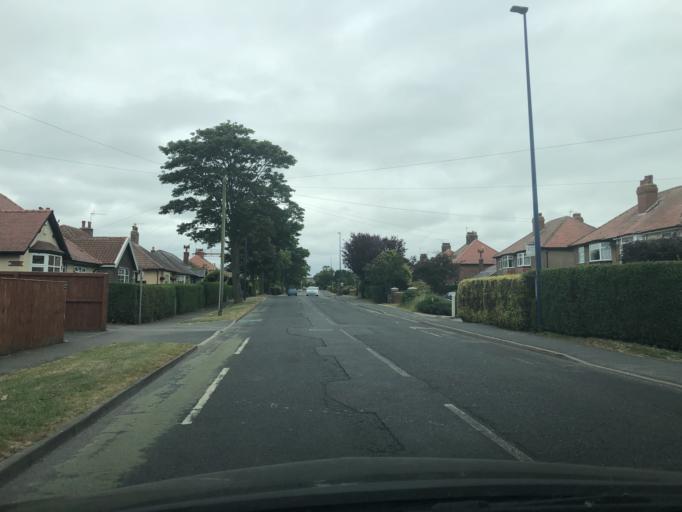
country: GB
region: England
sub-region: North Yorkshire
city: Filey
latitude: 54.2091
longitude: -0.2967
